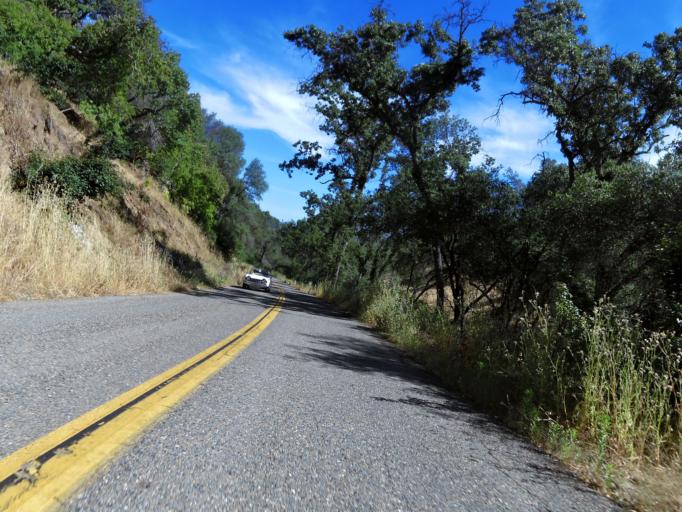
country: US
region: California
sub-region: Mariposa County
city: Mariposa
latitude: 37.3785
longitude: -119.9656
